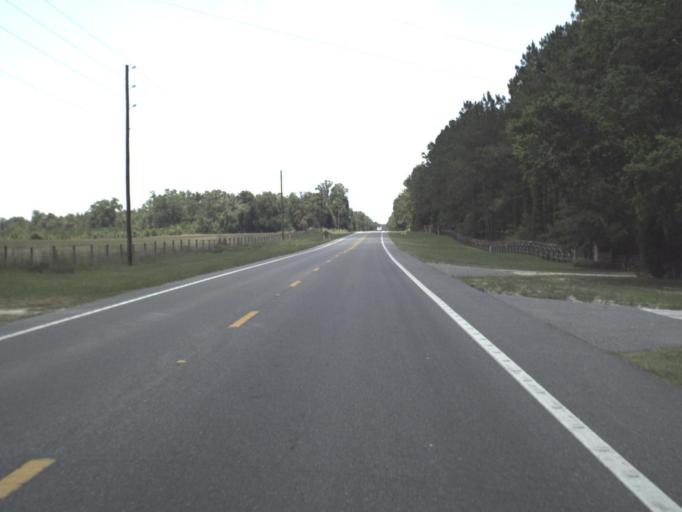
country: US
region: Florida
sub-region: Levy County
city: Williston
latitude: 29.4176
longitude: -82.4282
